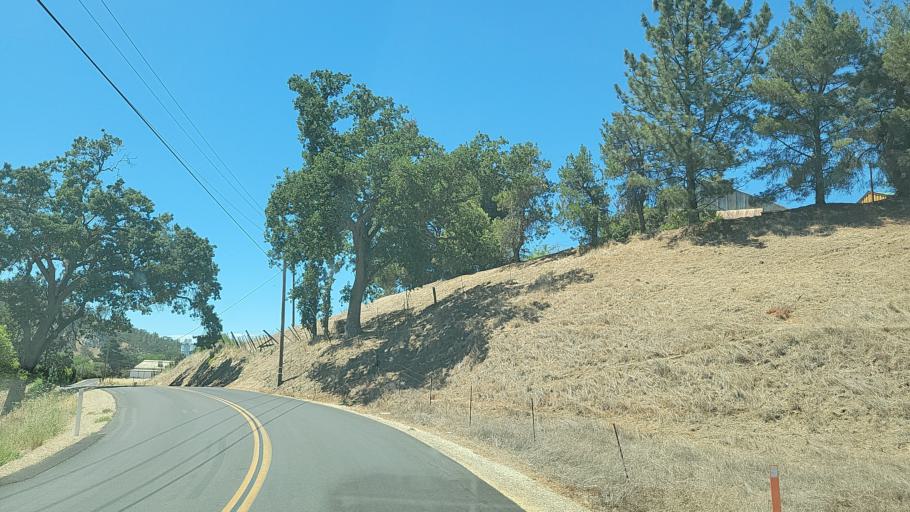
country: US
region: California
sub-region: San Luis Obispo County
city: Atascadero
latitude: 35.4907
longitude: -120.6404
